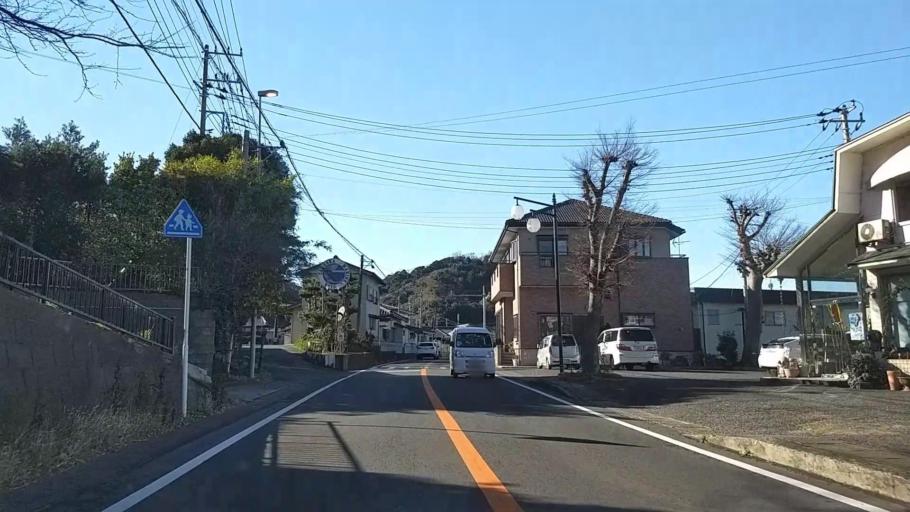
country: JP
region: Chiba
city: Futtsu
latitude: 35.1998
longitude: 139.8301
